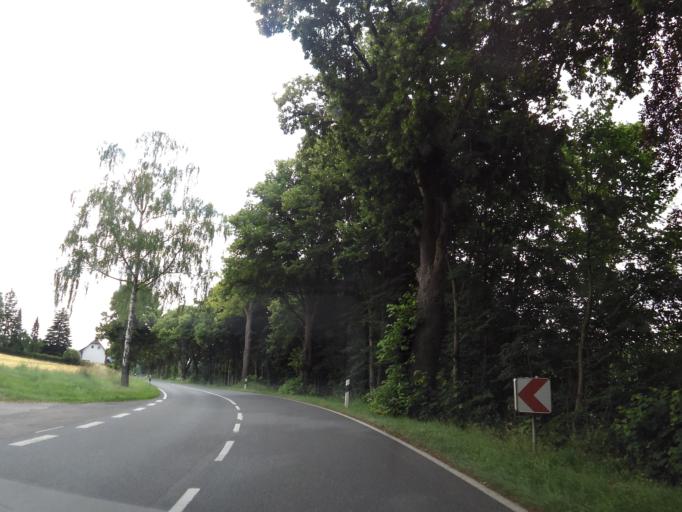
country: DE
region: North Rhine-Westphalia
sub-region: Regierungsbezirk Detmold
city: Hoexter
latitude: 51.7671
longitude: 9.4115
